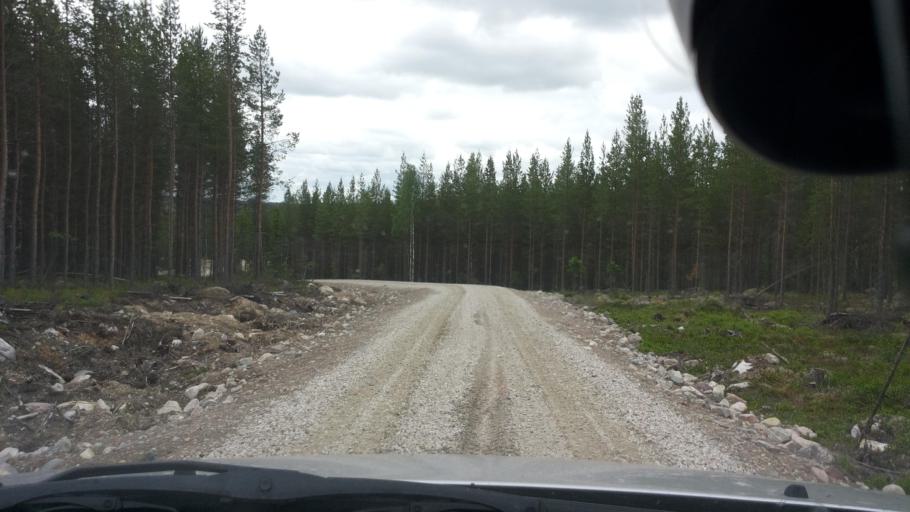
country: SE
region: Gaevleborg
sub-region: Ovanakers Kommun
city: Edsbyn
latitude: 61.4620
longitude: 15.2933
